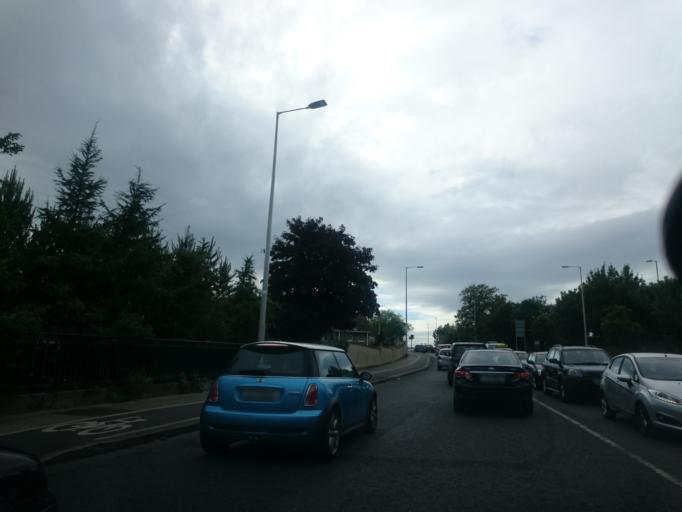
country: IE
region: Leinster
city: Dundrum
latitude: 53.2933
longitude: -6.2465
